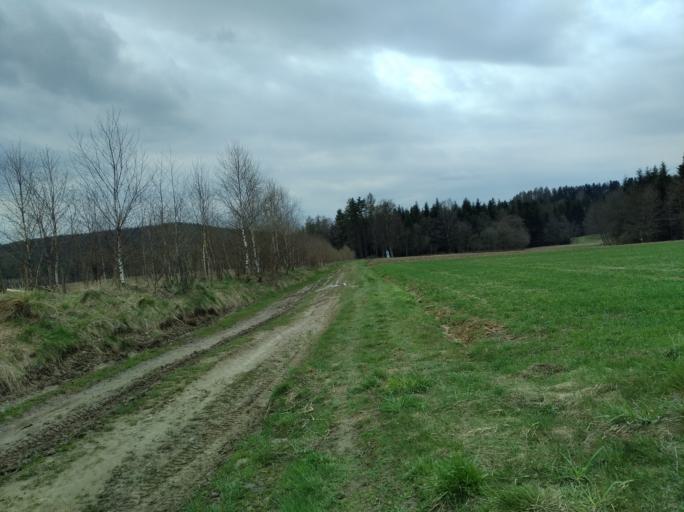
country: PL
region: Subcarpathian Voivodeship
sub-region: Powiat strzyzowski
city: Wysoka Strzyzowska
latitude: 49.8071
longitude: 21.7739
